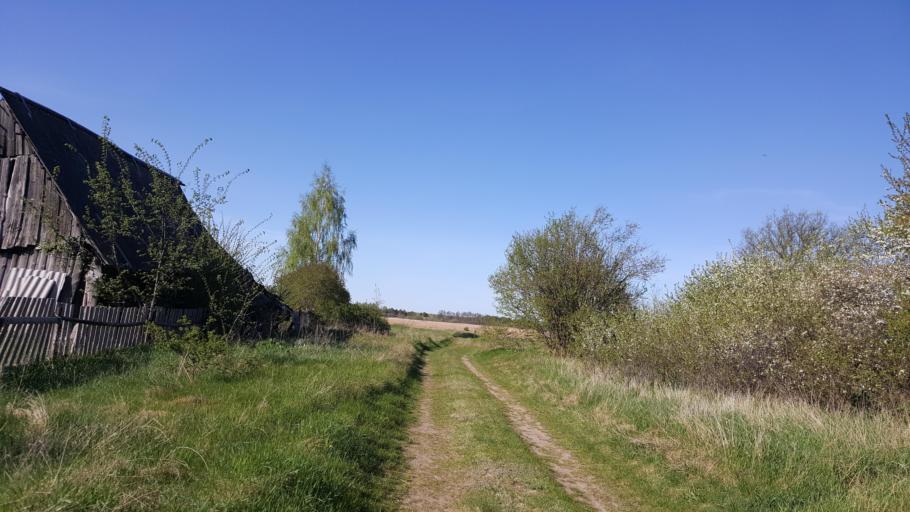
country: BY
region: Brest
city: Kamyanyets
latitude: 52.4403
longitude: 23.8945
